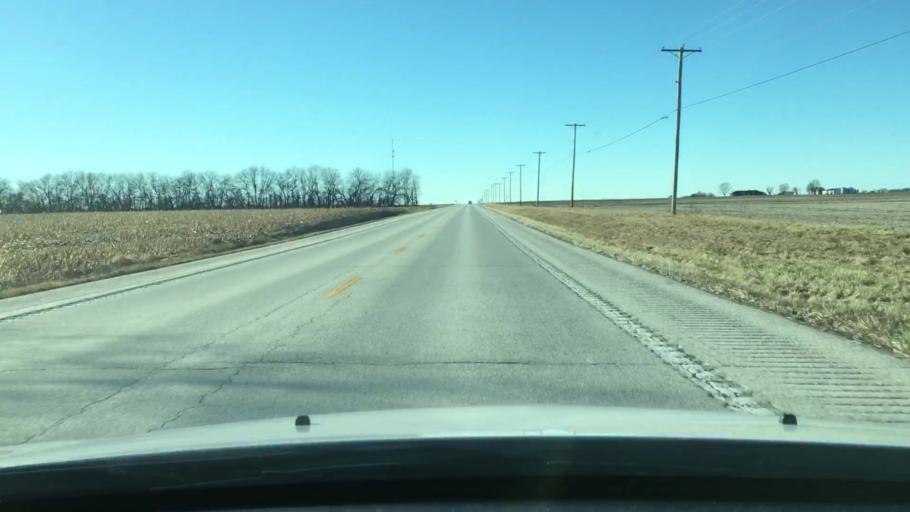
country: US
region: Missouri
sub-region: Pike County
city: Bowling Green
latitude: 39.3445
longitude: -91.2871
